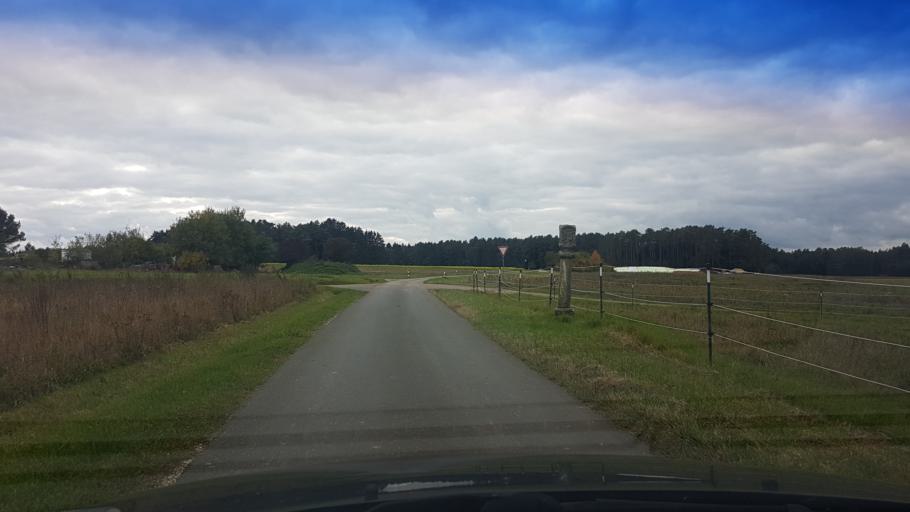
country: DE
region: Bavaria
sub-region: Upper Franconia
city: Stadelhofen
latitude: 50.0064
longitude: 11.2363
